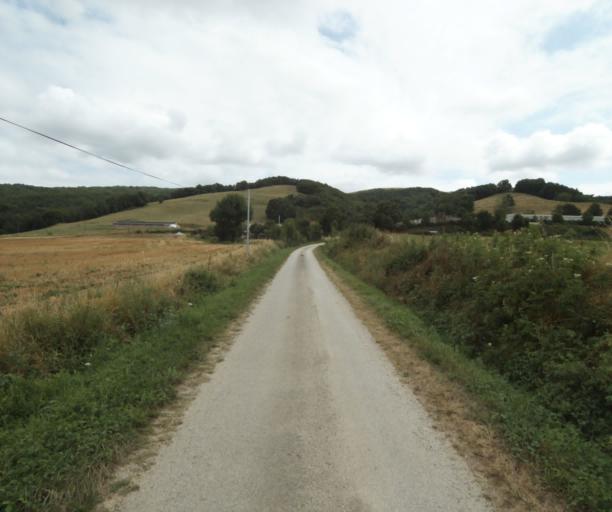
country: FR
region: Midi-Pyrenees
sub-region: Departement du Tarn
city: Soreze
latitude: 43.4556
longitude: 2.0794
